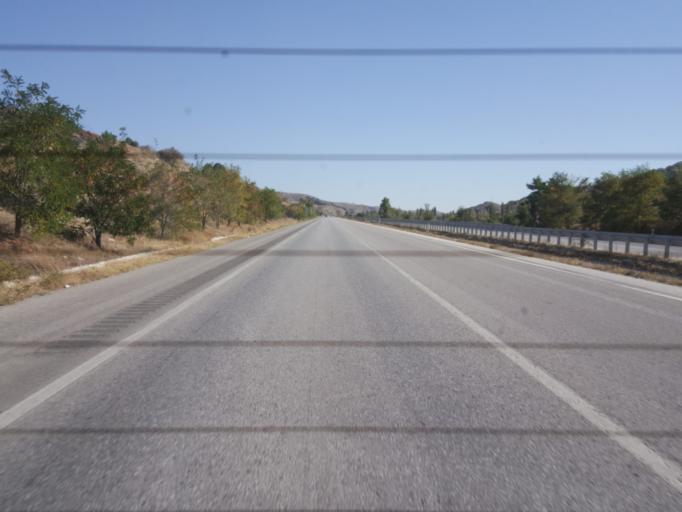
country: TR
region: Corum
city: Sungurlu
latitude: 40.1927
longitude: 34.5048
